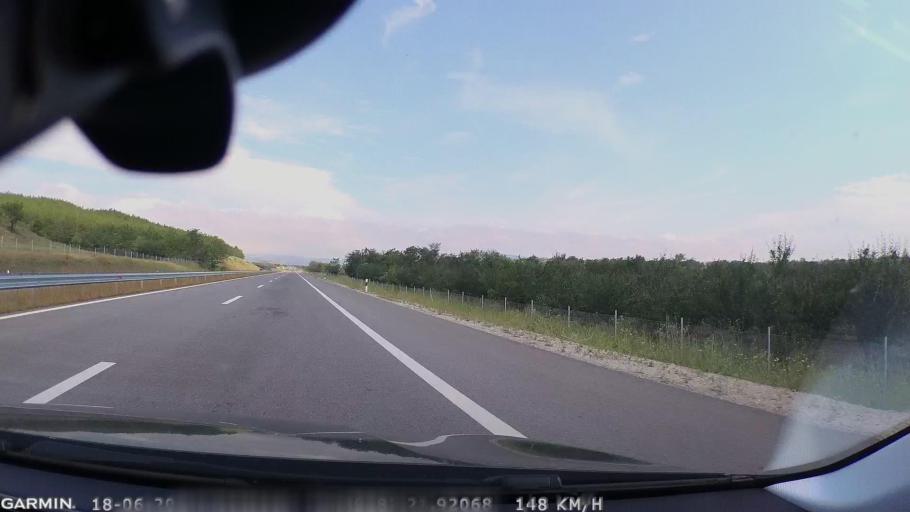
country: MK
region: Sveti Nikole
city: Sveti Nikole
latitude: 41.8981
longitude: 21.9189
